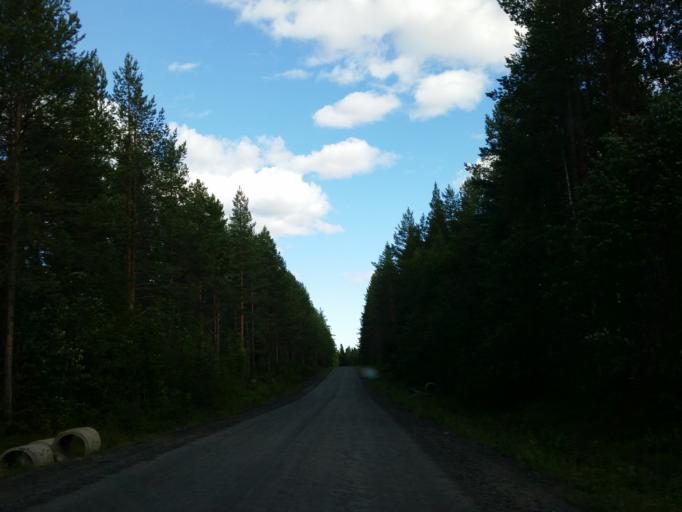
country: SE
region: Vaesterbotten
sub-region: Robertsfors Kommun
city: Robertsfors
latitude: 64.1409
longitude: 20.8583
